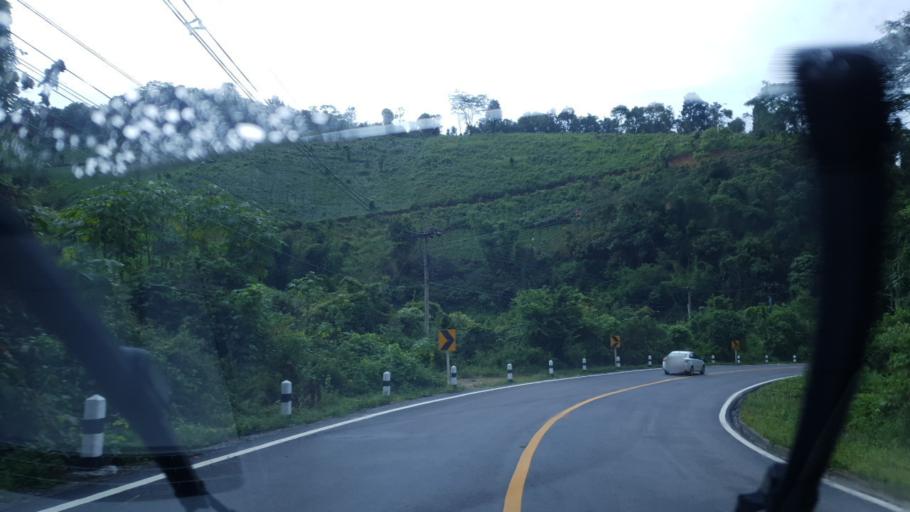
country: TH
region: Mae Hong Son
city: Ban Huai I Huak
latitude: 18.1447
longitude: 98.1149
